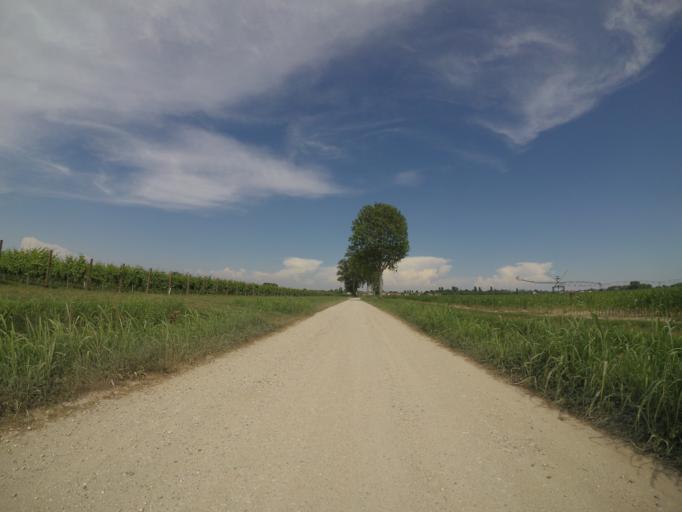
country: IT
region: Friuli Venezia Giulia
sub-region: Provincia di Udine
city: Camino al Tagliamento
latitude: 45.9266
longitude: 12.9282
